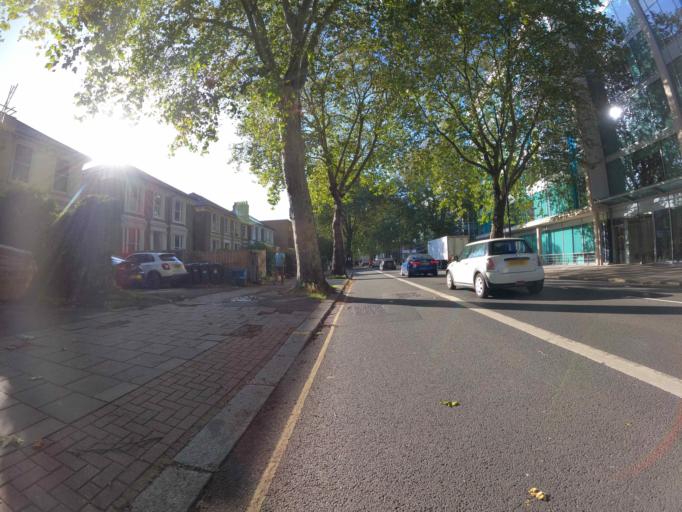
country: GB
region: England
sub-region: Greater London
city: Acton
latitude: 51.4922
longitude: -0.2769
